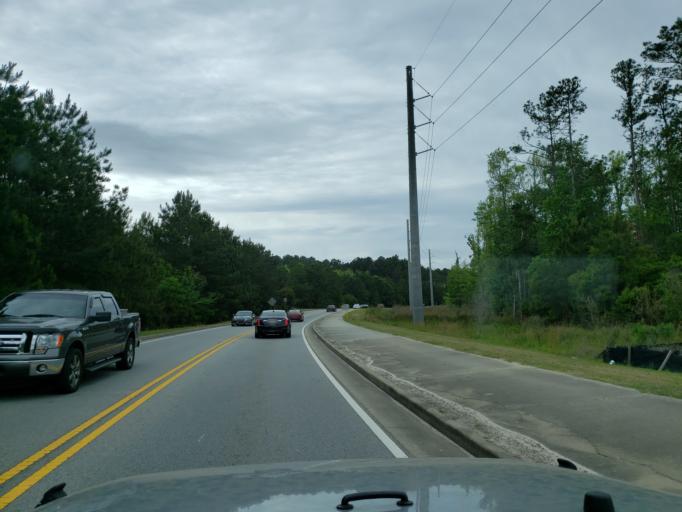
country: US
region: Georgia
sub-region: Chatham County
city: Pooler
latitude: 32.1608
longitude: -81.2329
